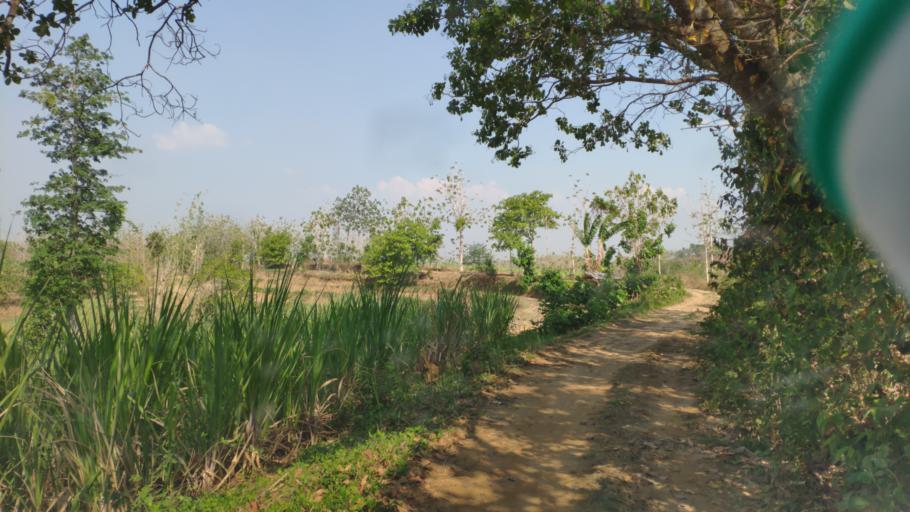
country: ID
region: Central Java
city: Ngapus
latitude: -6.9284
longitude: 111.2104
